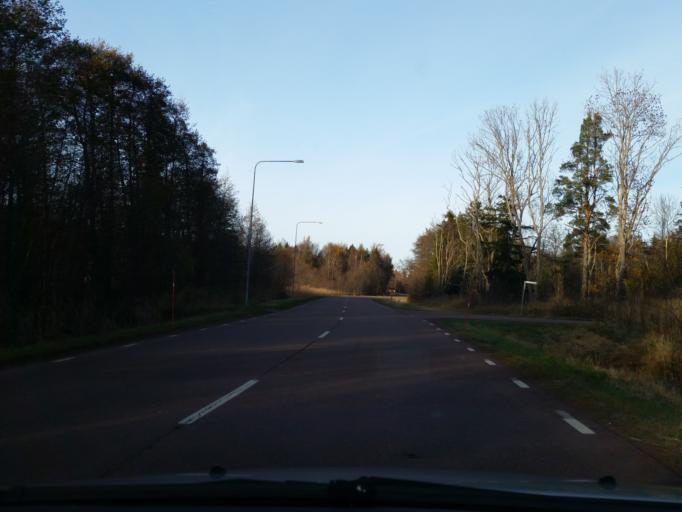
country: AX
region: Mariehamns stad
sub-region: Mariehamn
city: Mariehamn
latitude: 60.1162
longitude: 19.9150
